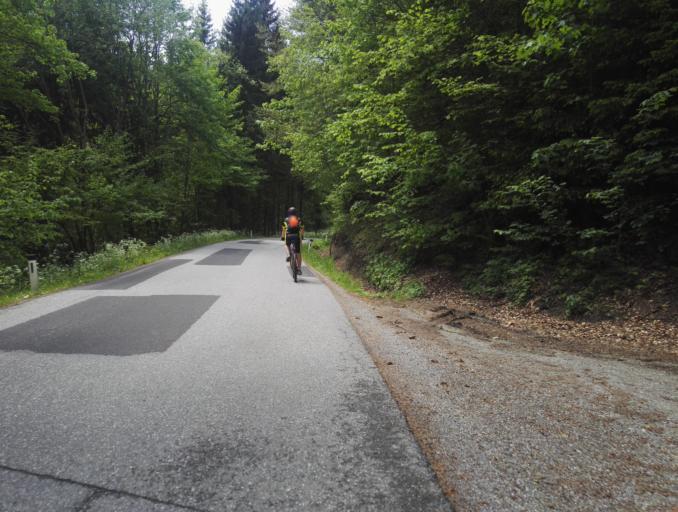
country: AT
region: Styria
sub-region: Politischer Bezirk Weiz
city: Stenzengreith
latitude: 47.2115
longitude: 15.4830
